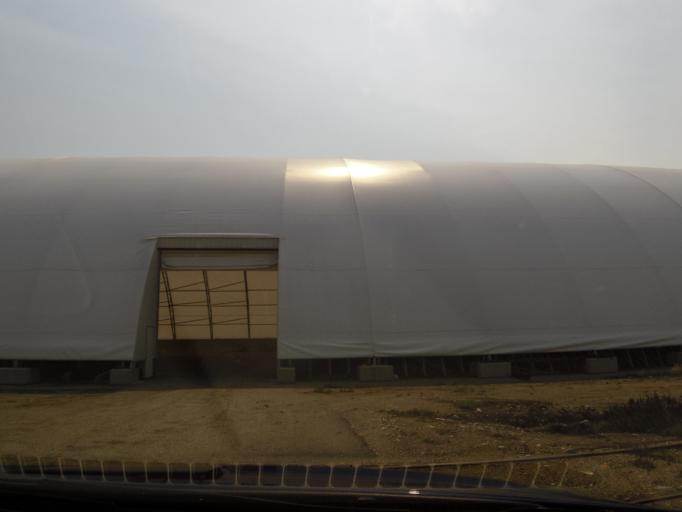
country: US
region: South Dakota
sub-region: Roberts County
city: Sisseton
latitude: 45.8555
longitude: -97.1081
